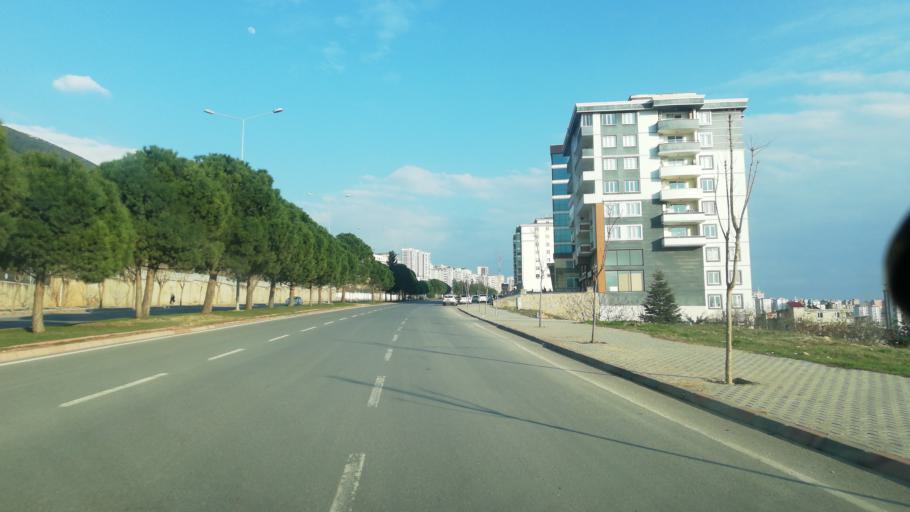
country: TR
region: Kahramanmaras
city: Kahramanmaras
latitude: 37.5999
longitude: 36.8333
